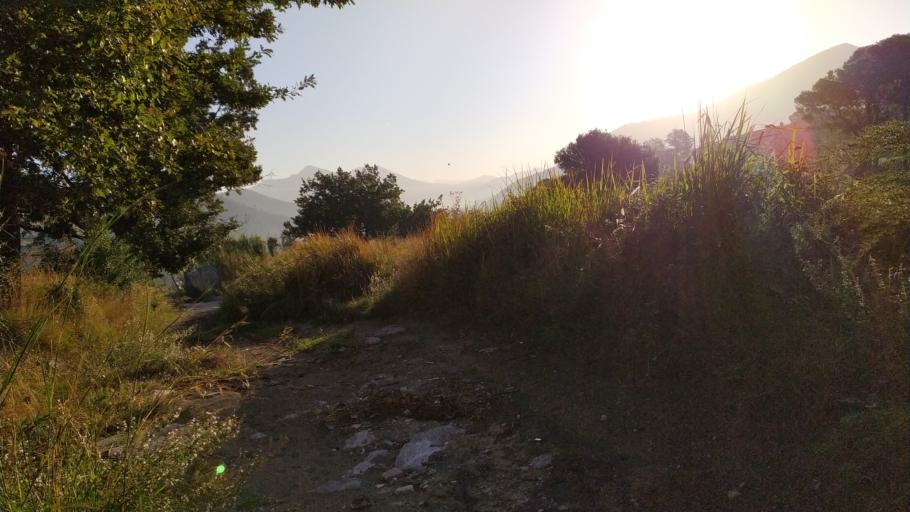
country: IT
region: Campania
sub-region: Provincia di Salerno
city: Lanzara
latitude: 40.7761
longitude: 14.6643
